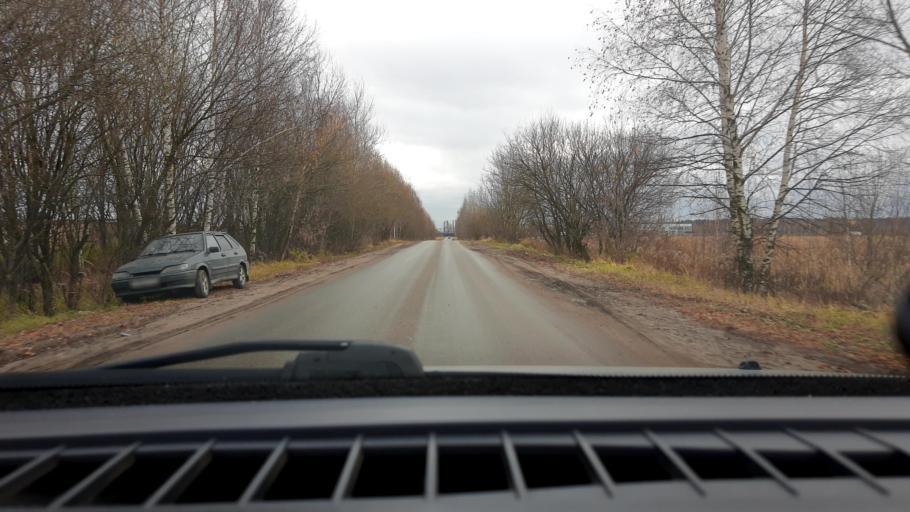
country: RU
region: Nizjnij Novgorod
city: Afonino
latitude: 56.1984
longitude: 44.1349
